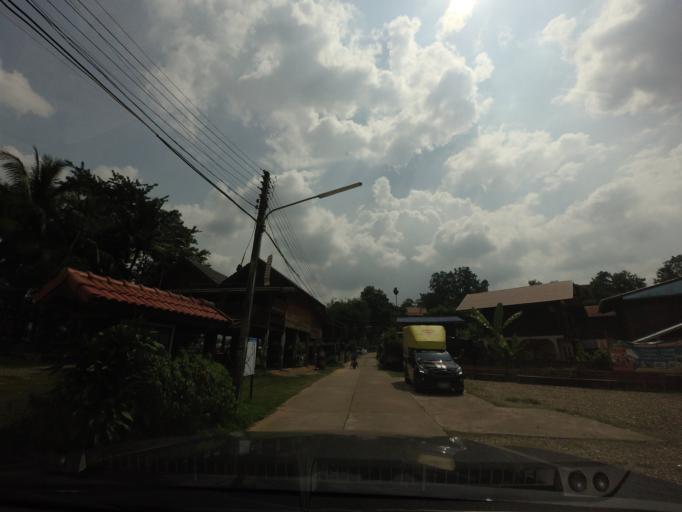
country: TH
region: Nan
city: Pua
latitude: 19.1668
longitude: 100.9343
